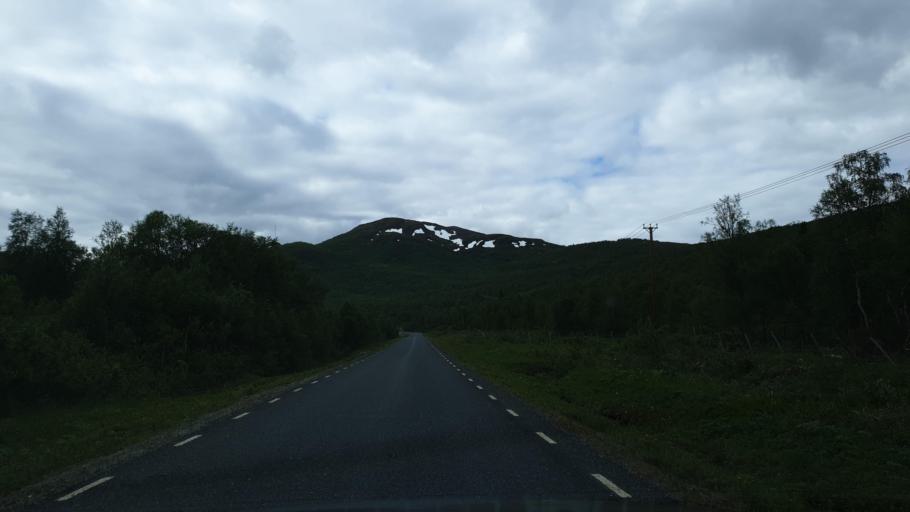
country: NO
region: Nordland
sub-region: Hattfjelldal
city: Hattfjelldal
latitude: 65.4240
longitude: 14.6589
